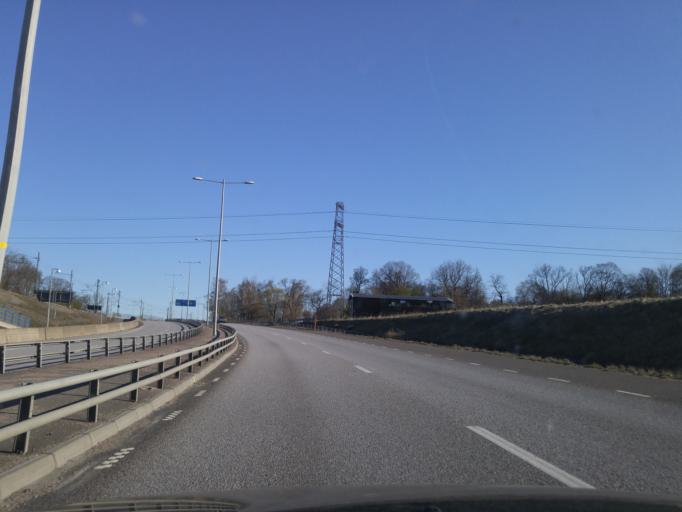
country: SE
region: Vaestra Goetaland
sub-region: Goteborg
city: Hammarkullen
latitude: 57.7585
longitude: 12.0048
